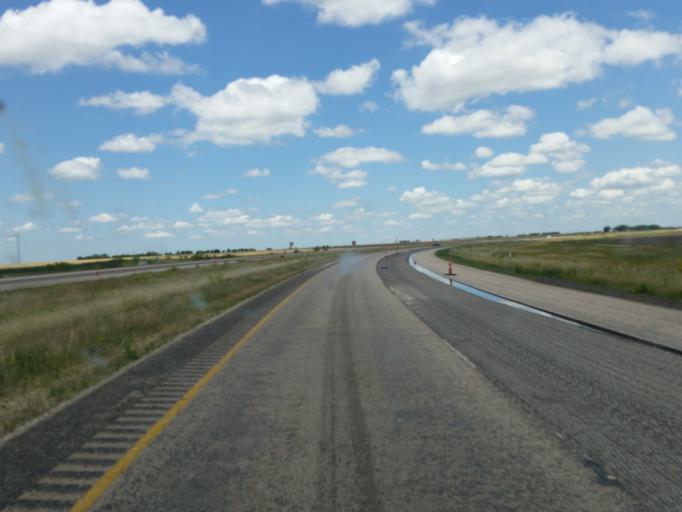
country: US
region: Texas
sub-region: Nolan County
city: Roscoe
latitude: 32.4558
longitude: -100.5368
